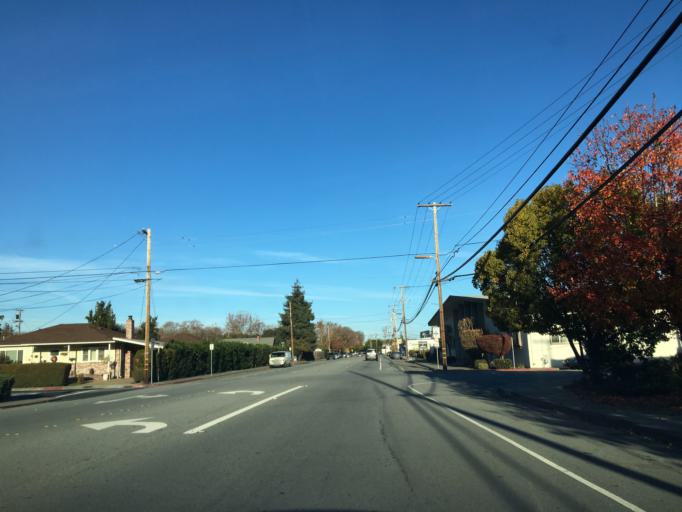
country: US
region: California
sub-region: San Mateo County
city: Redwood City
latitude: 37.4943
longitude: -122.2368
